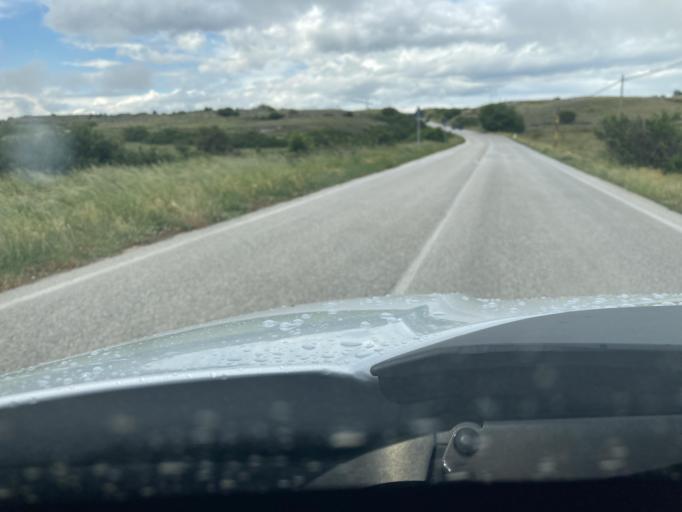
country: IT
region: Abruzzo
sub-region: Provincia dell' Aquila
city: Rocca di Mezzo
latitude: 42.2286
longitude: 13.5331
